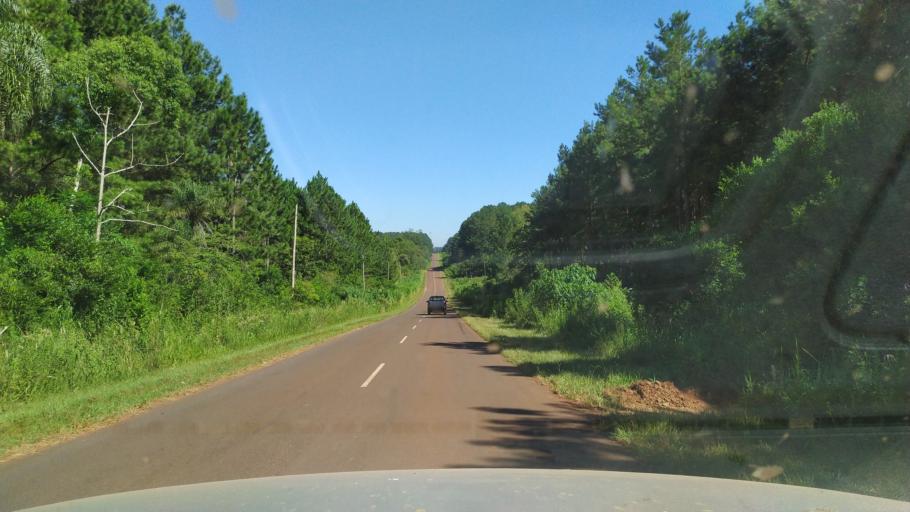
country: AR
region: Misiones
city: Caraguatay
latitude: -26.6685
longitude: -54.7280
